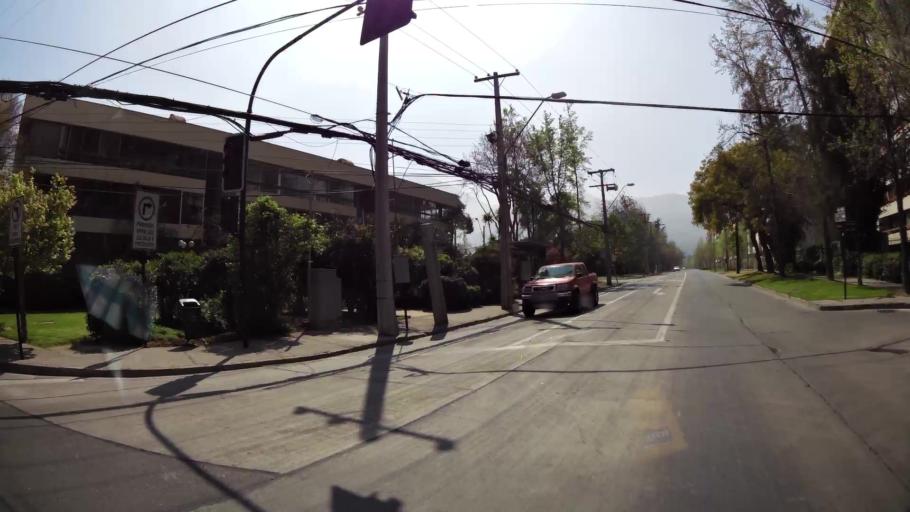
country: CL
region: Santiago Metropolitan
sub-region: Provincia de Santiago
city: Villa Presidente Frei, Nunoa, Santiago, Chile
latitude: -33.3855
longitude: -70.5704
